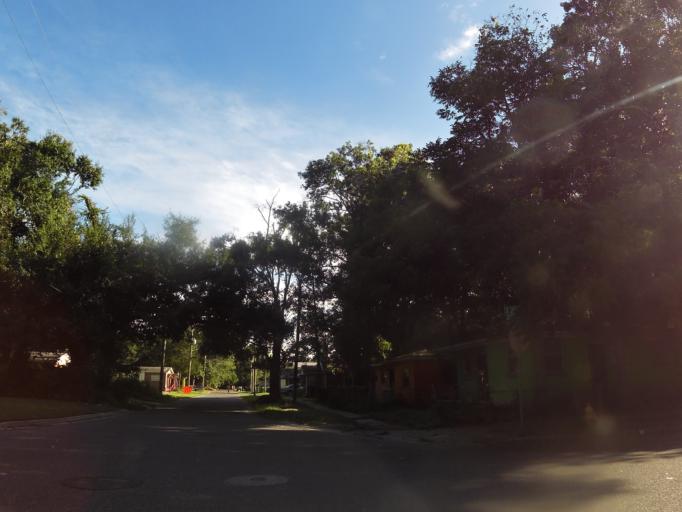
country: US
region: Florida
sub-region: Duval County
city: Jacksonville
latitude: 30.3507
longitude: -81.6898
